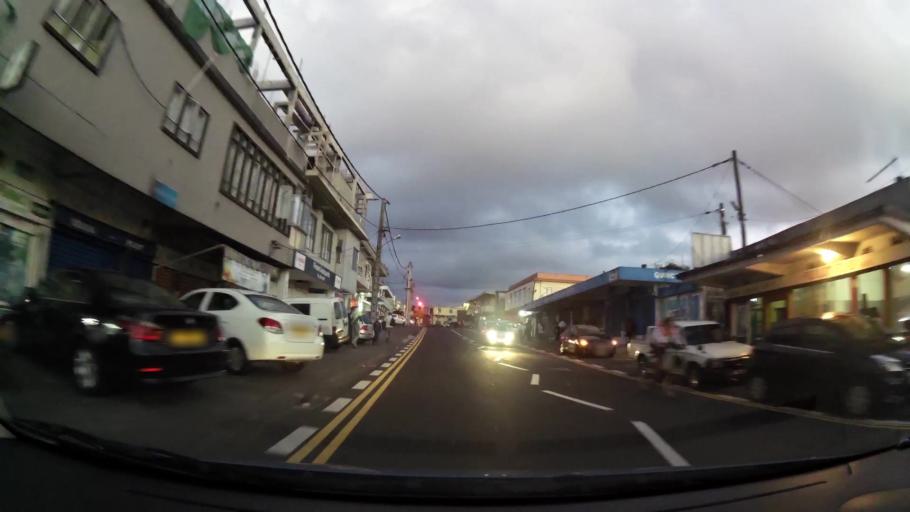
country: MU
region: Plaines Wilhems
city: Curepipe
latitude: -20.3023
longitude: 57.5217
